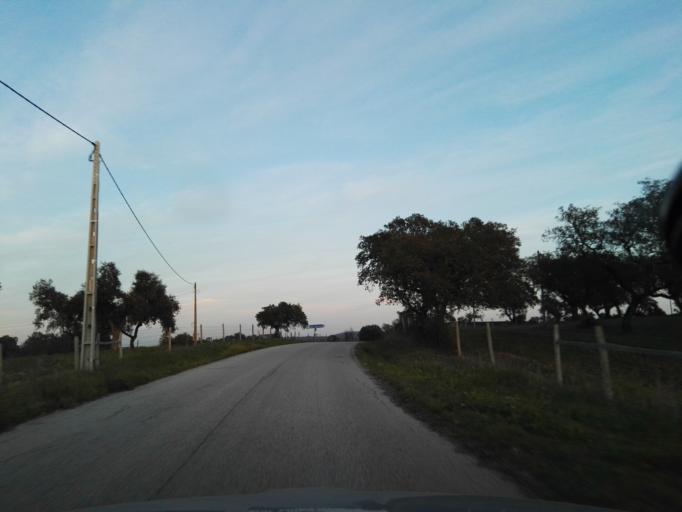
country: PT
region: Evora
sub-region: Montemor-O-Novo
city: Montemor-o-Novo
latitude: 38.7626
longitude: -8.1866
